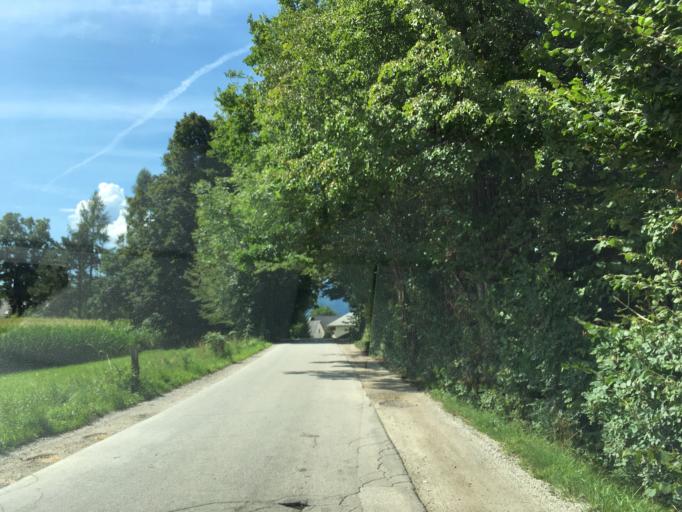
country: SI
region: Radovljica
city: Lesce
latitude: 46.3728
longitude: 14.1678
